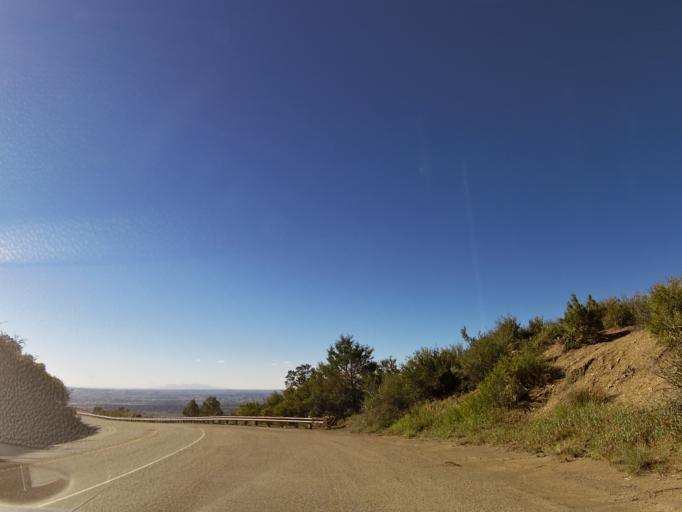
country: US
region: Colorado
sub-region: Montezuma County
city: Mancos
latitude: 37.3196
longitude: -108.4172
